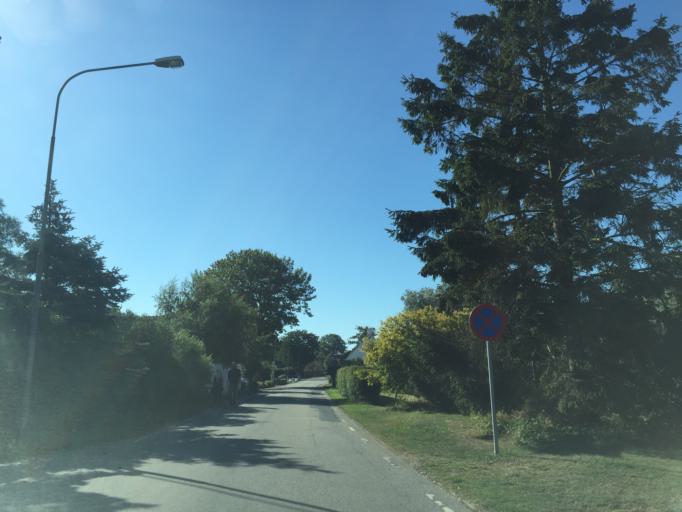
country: SE
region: Skane
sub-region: Ystads Kommun
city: Kopingebro
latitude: 55.3877
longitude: 14.0643
